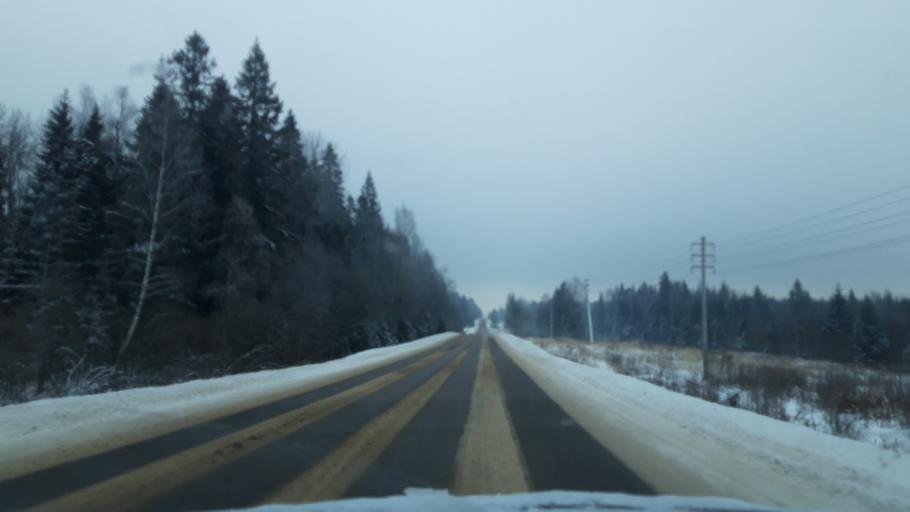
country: RU
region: Moskovskaya
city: Avtopoligon
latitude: 56.2641
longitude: 37.3021
